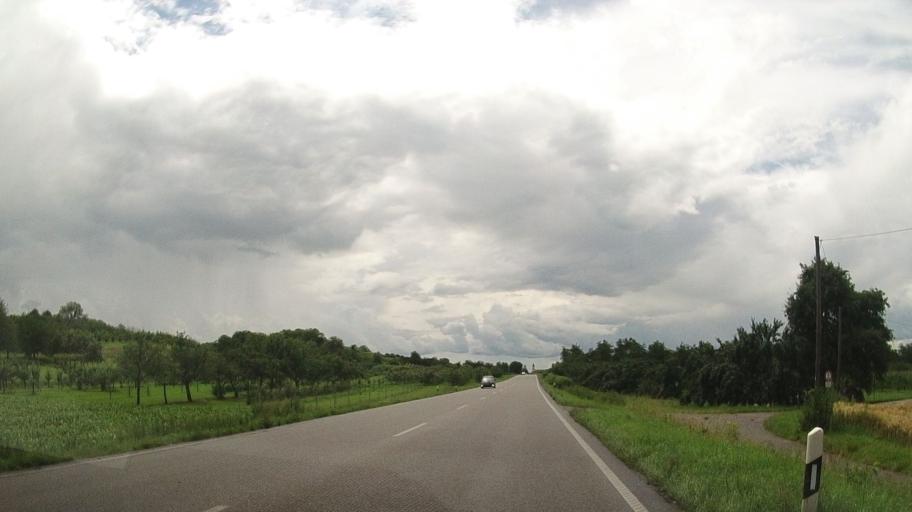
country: DE
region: Baden-Wuerttemberg
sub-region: Freiburg Region
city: Renchen
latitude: 48.5997
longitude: 8.0263
